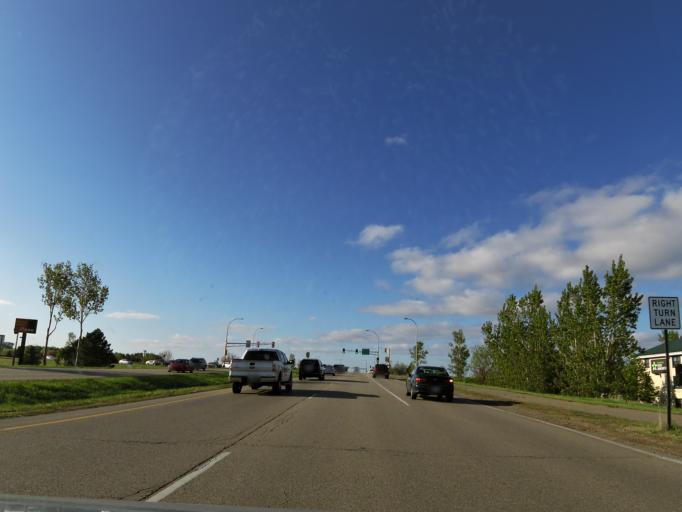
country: US
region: Minnesota
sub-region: Washington County
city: Woodbury
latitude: 44.9478
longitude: -92.9089
